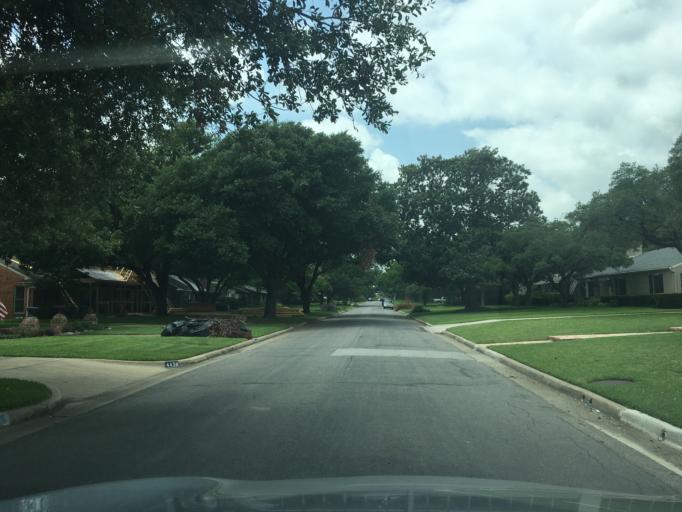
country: US
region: Texas
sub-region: Dallas County
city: Addison
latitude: 32.9043
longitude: -96.8325
